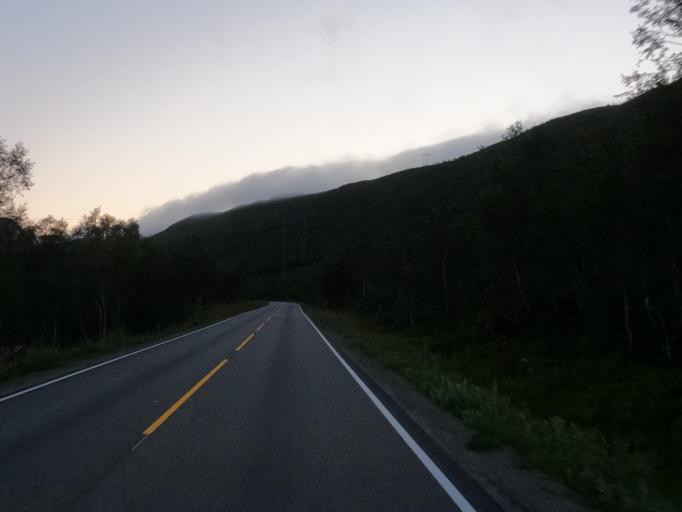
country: NO
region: Nordland
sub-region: Lodingen
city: Lodingen
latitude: 68.5290
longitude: 15.8188
